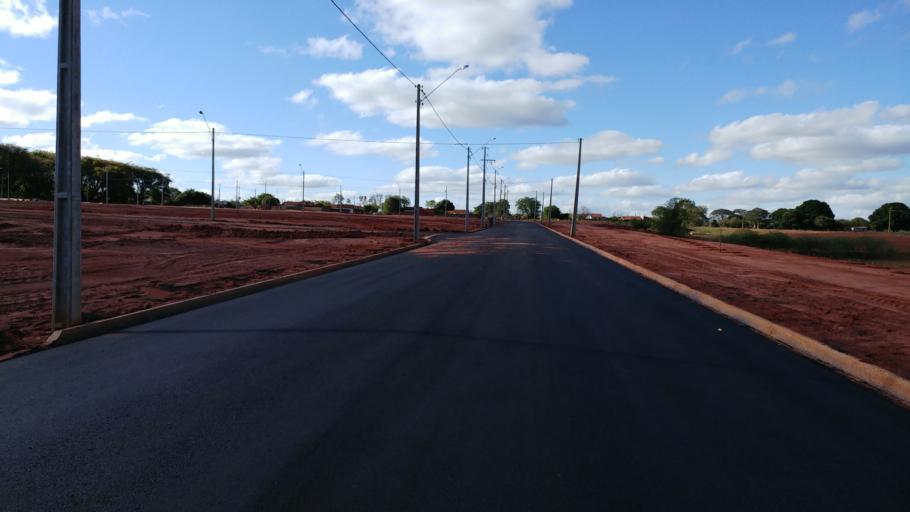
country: BR
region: Sao Paulo
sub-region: Paraguacu Paulista
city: Paraguacu Paulista
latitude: -22.4389
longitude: -50.5755
